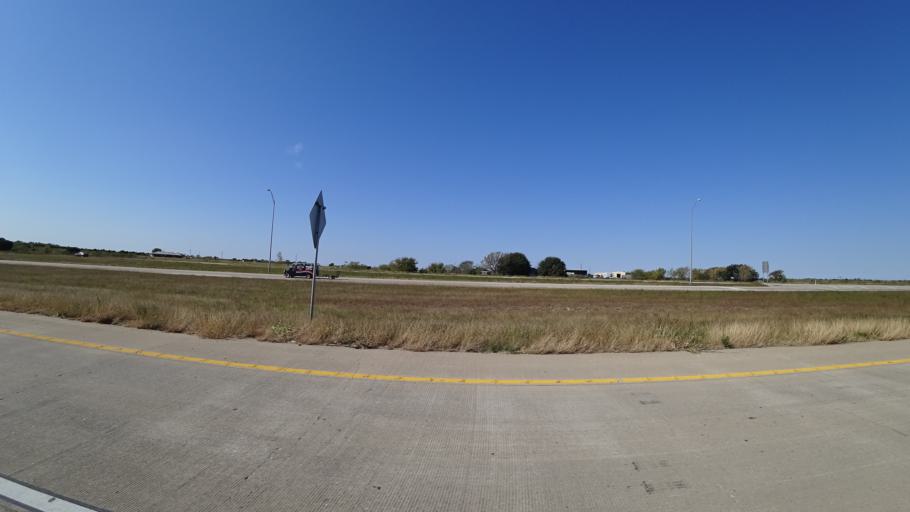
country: US
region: Texas
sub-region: Travis County
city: Manor
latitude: 30.3498
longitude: -97.5934
